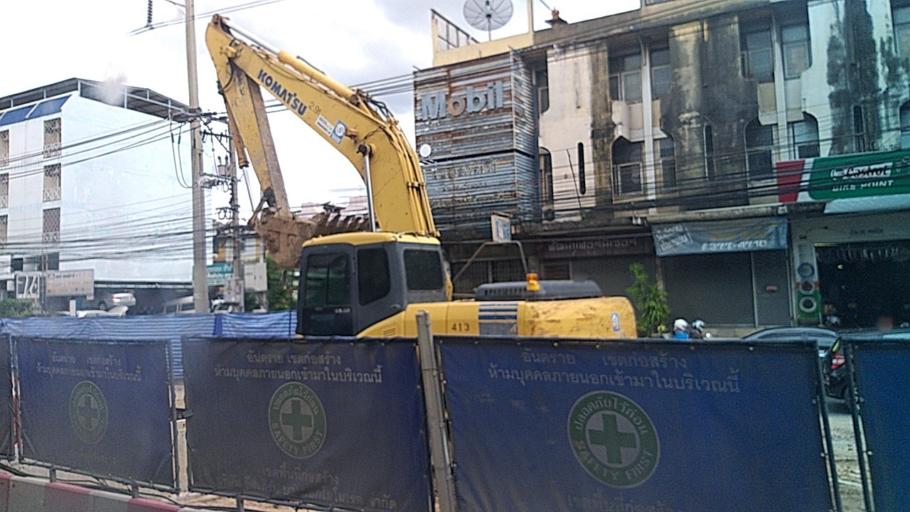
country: TH
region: Bangkok
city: Bang Kapi
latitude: 13.7590
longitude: 100.6450
